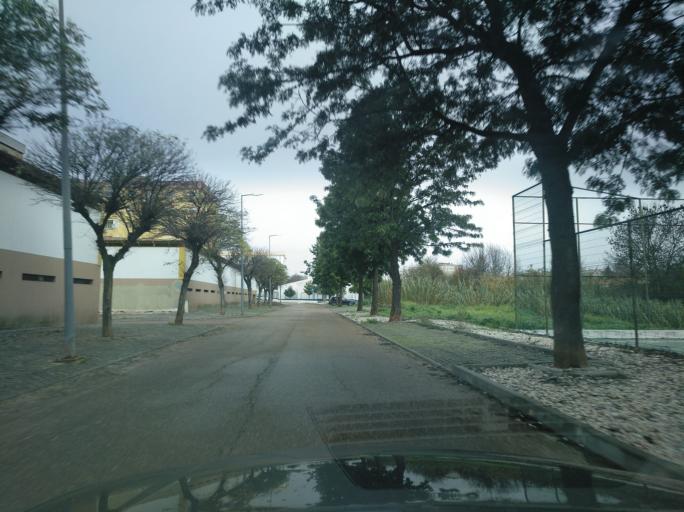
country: PT
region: Portalegre
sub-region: Elvas
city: Elvas
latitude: 38.8674
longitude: -7.1705
